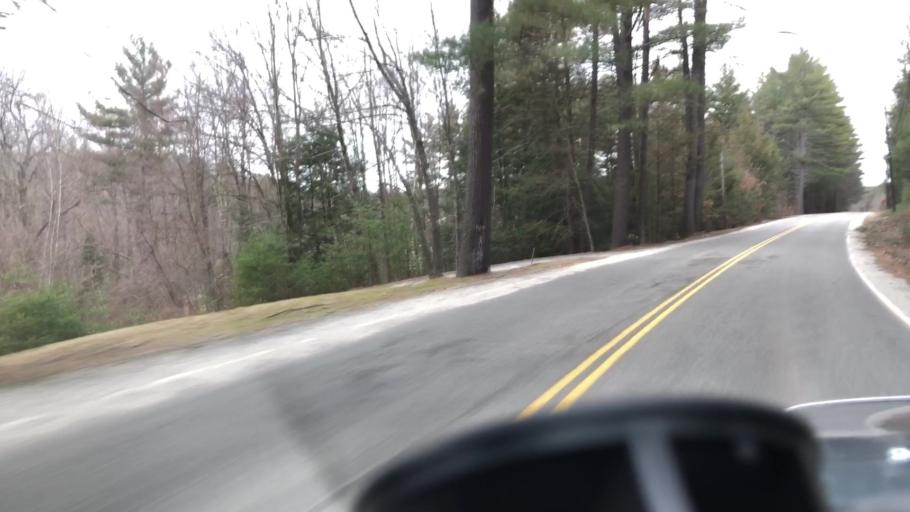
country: US
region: Massachusetts
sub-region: Hampshire County
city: Southampton
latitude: 42.2127
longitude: -72.7335
